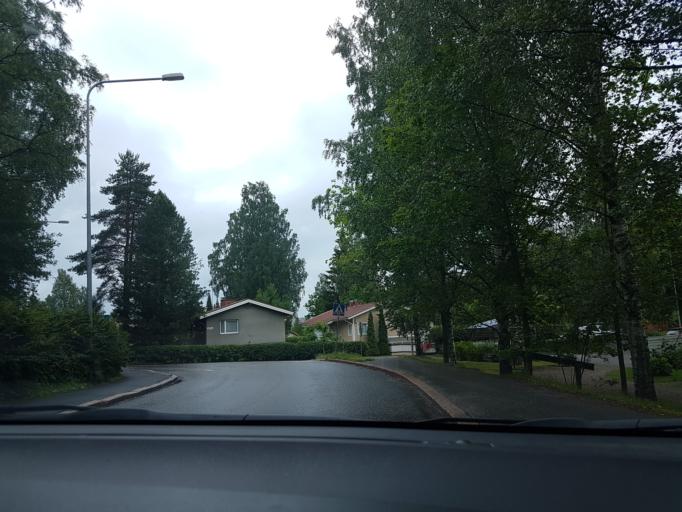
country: FI
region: Uusimaa
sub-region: Helsinki
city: Vantaa
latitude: 60.2267
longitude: 25.1032
